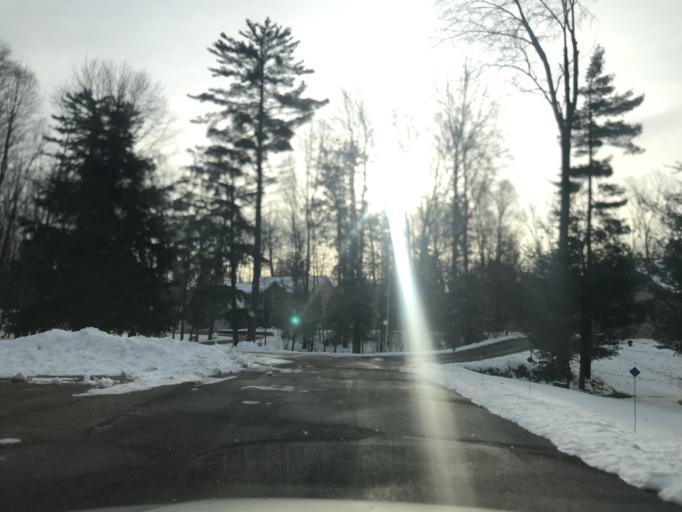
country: US
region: Wisconsin
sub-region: Brown County
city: Suamico
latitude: 44.6855
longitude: -88.0565
